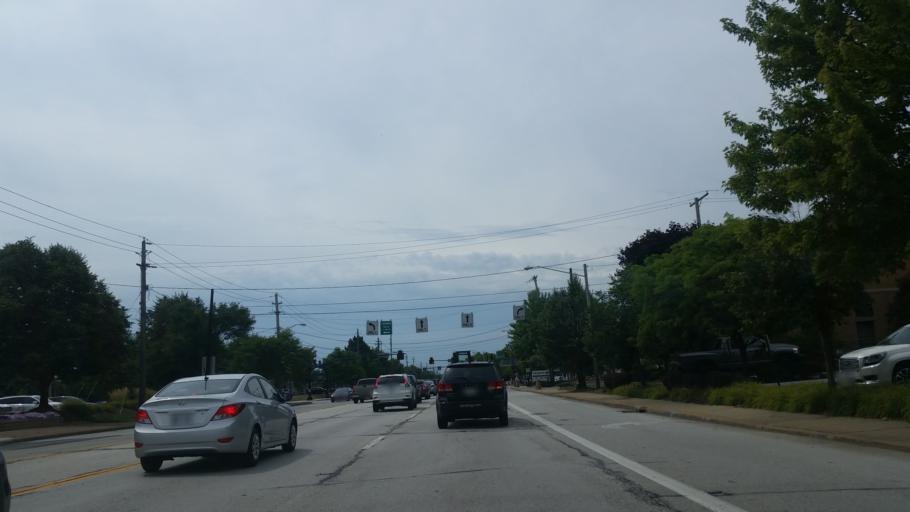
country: US
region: Ohio
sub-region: Cuyahoga County
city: Solon
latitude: 41.3932
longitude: -81.4378
